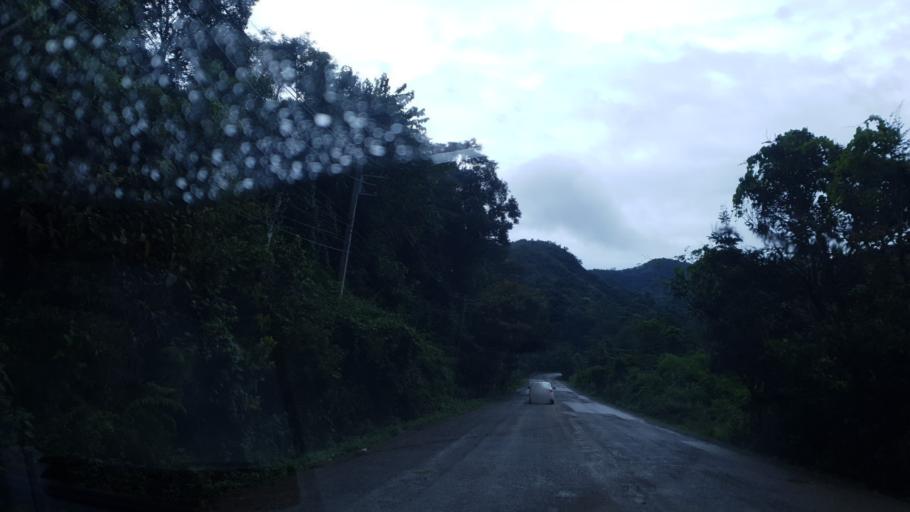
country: TH
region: Mae Hong Son
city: Ban Huai I Huak
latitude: 18.1491
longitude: 98.1248
